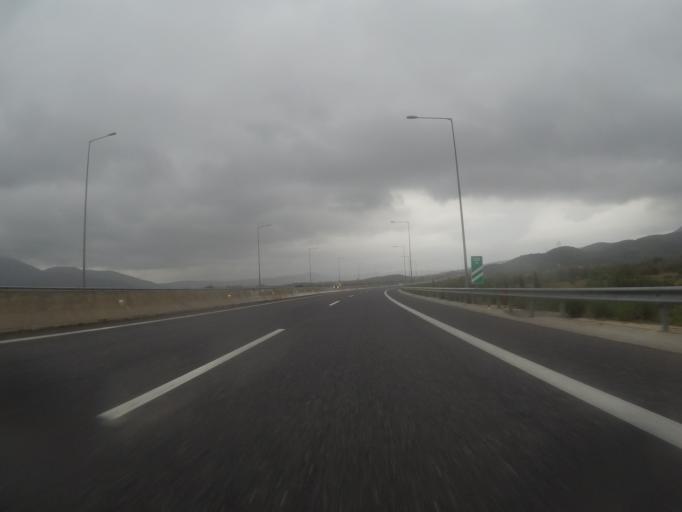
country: GR
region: Peloponnese
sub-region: Nomos Arkadias
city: Megalopoli
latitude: 37.3869
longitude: 22.2689
